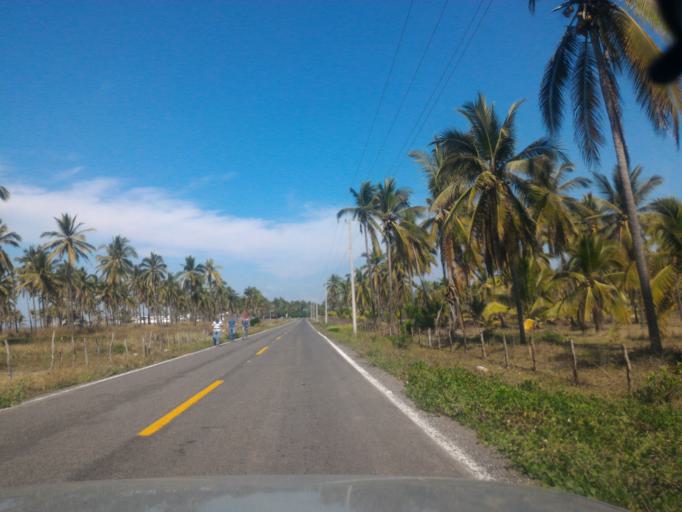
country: MX
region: Colima
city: Armeria
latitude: 18.8533
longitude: -103.9575
